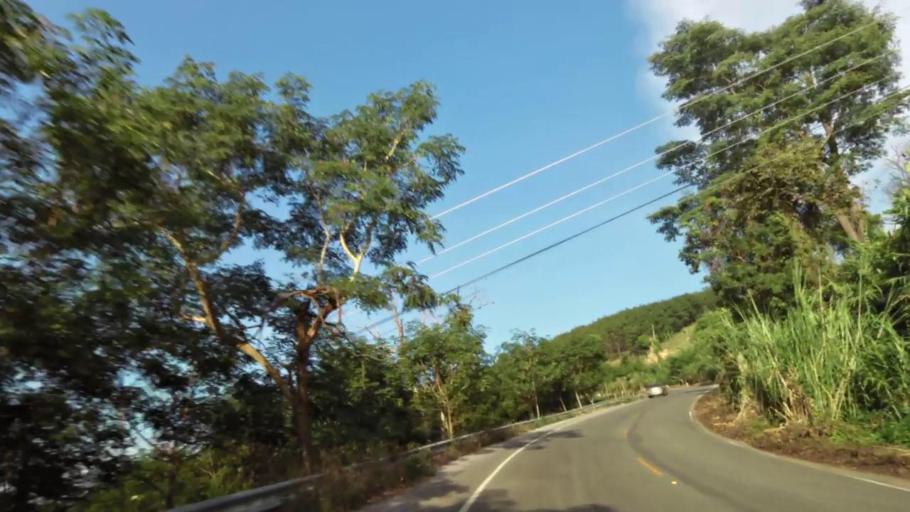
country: TH
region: Chiang Rai
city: Khun Tan
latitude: 19.8643
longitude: 100.4188
